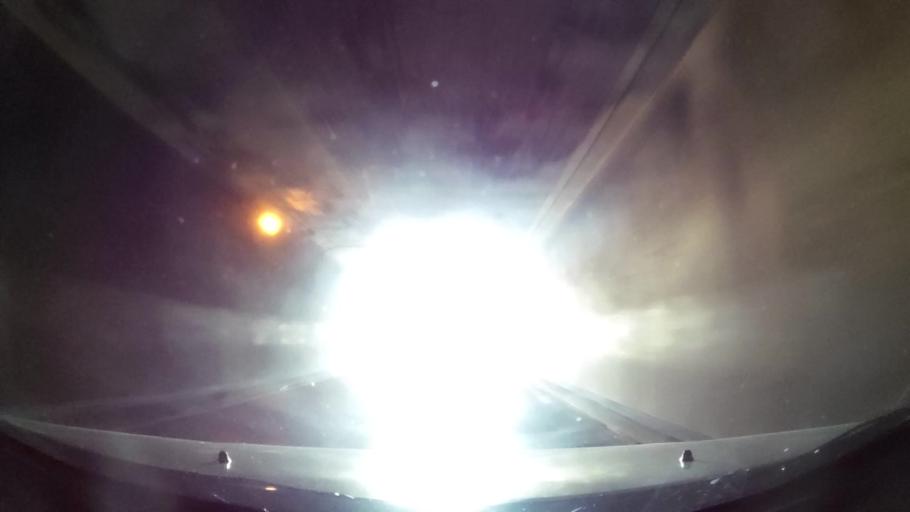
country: UY
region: Montevideo
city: Montevideo
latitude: -34.8940
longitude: -56.1640
